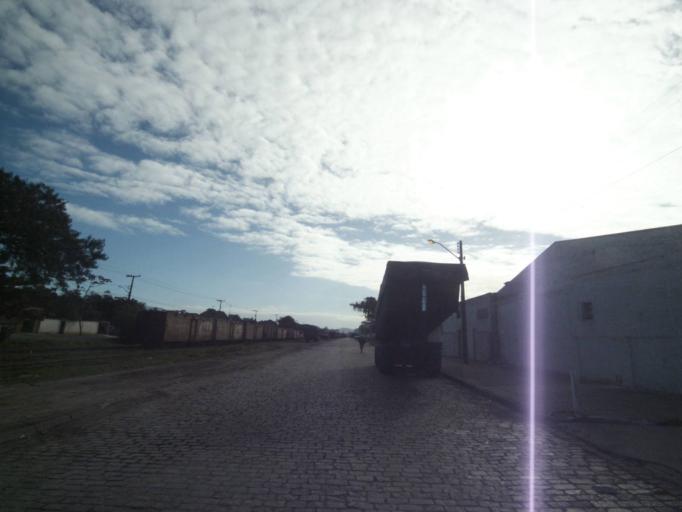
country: BR
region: Parana
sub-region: Paranagua
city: Paranagua
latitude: -25.5240
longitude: -48.5284
